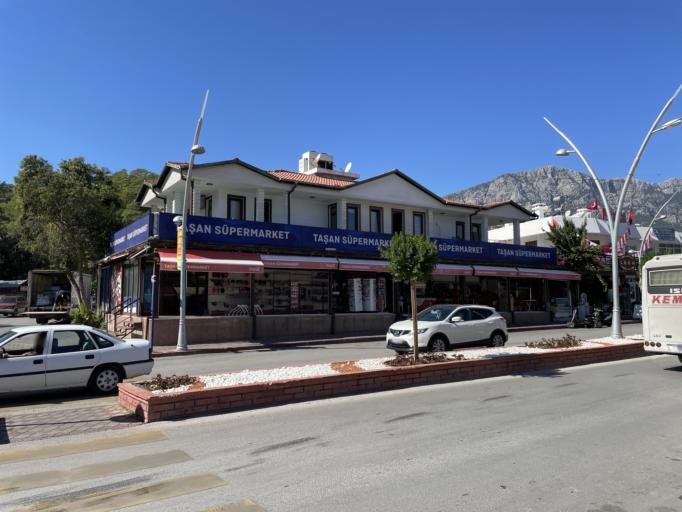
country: TR
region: Antalya
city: Kemer
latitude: 36.5969
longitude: 30.5634
